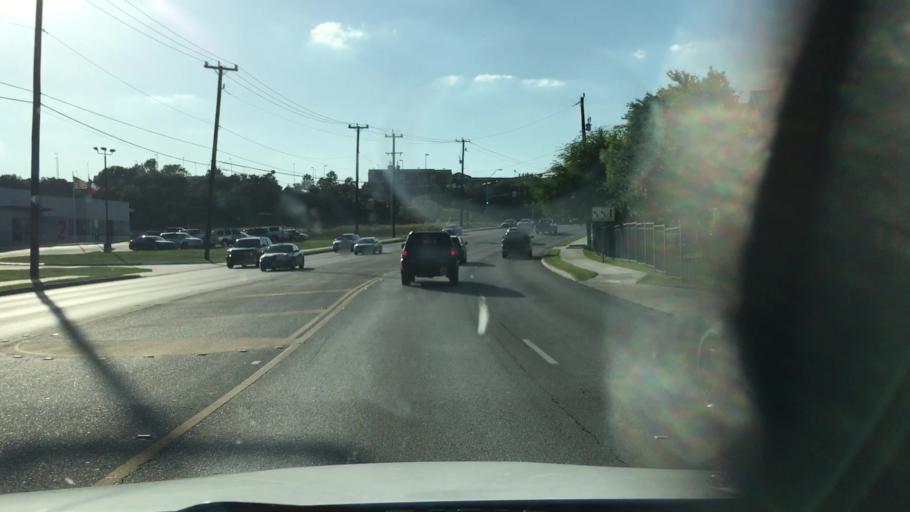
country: US
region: Texas
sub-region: Bexar County
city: Timberwood Park
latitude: 29.6554
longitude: -98.4307
